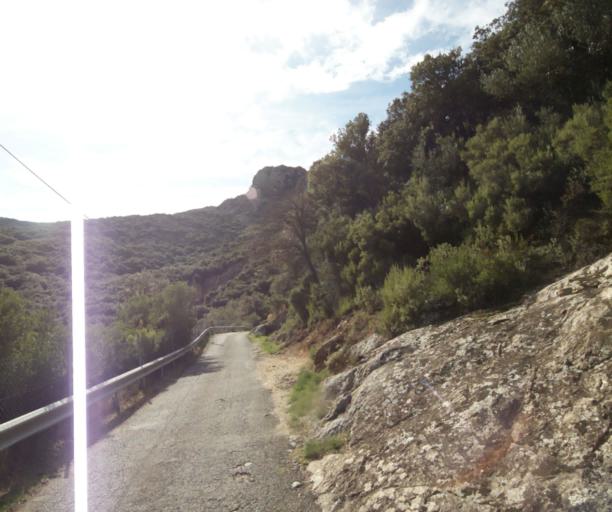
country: FR
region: Languedoc-Roussillon
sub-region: Departement des Pyrenees-Orientales
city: Sorede
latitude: 42.5187
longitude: 2.9882
